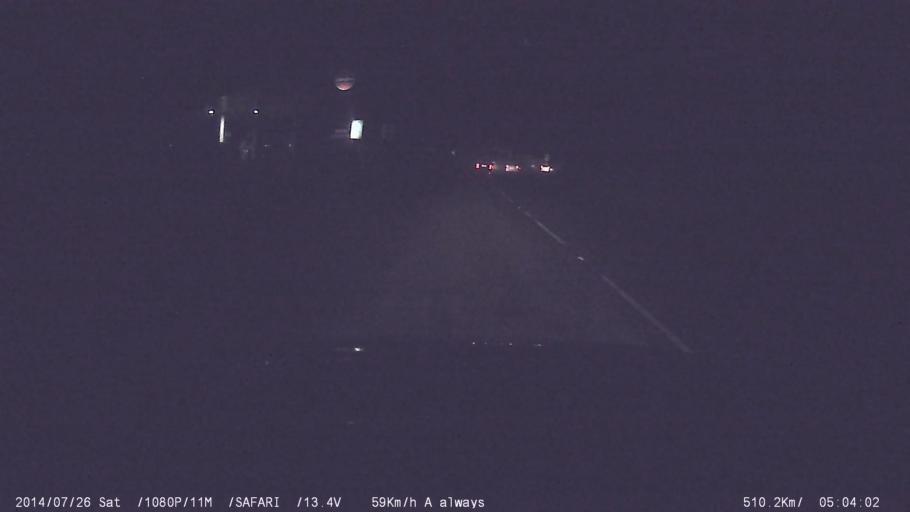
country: IN
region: Kerala
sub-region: Ernakulam
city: Perumbavoor
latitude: 10.0966
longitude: 76.4930
